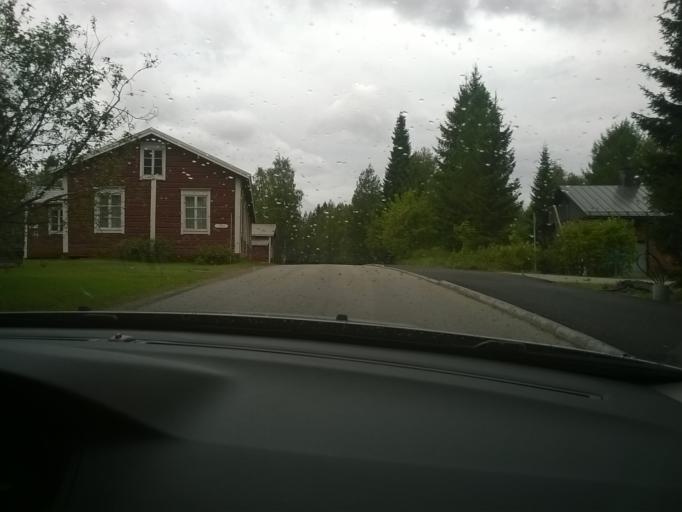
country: FI
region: Kainuu
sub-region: Kehys-Kainuu
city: Kuhmo
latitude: 64.1254
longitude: 29.5040
